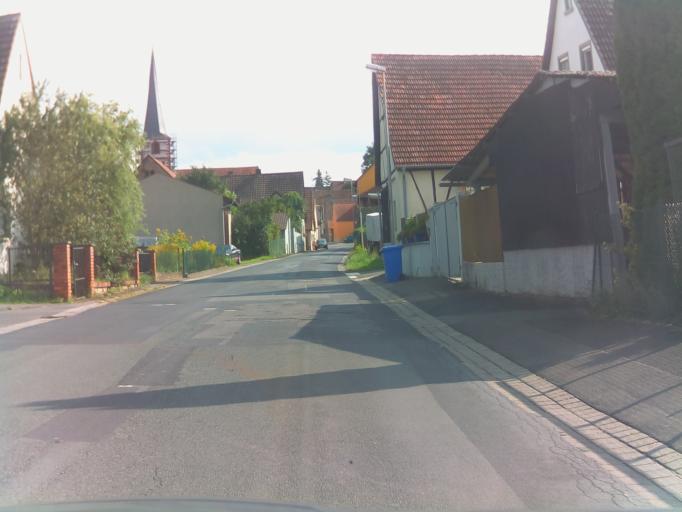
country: DE
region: Bavaria
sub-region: Regierungsbezirk Unterfranken
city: Zellingen
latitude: 49.8704
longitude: 9.7995
